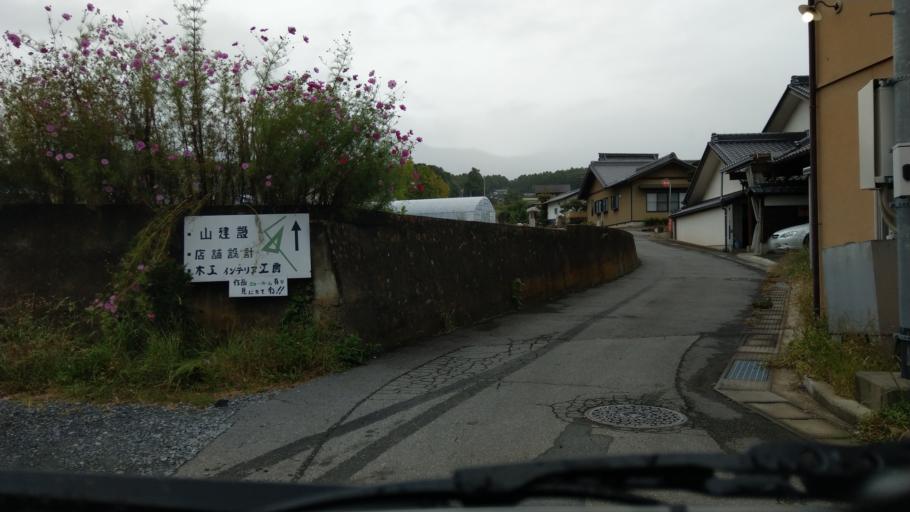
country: JP
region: Nagano
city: Komoro
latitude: 36.3334
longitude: 138.4510
